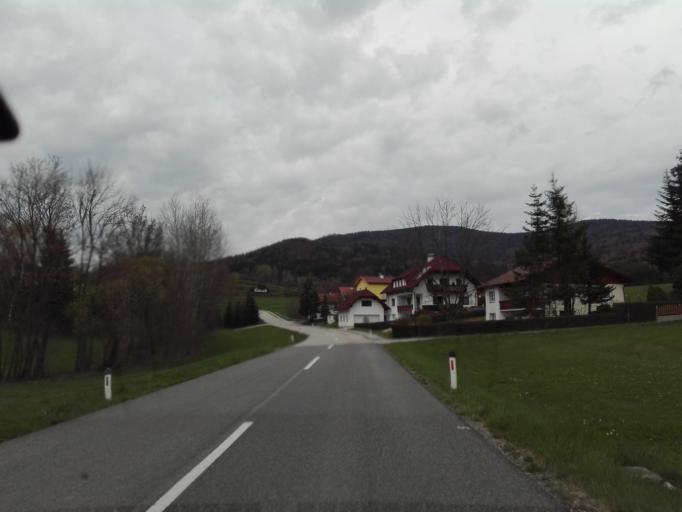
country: AT
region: Upper Austria
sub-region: Politischer Bezirk Rohrbach
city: Ulrichsberg
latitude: 48.7028
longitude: 13.9052
